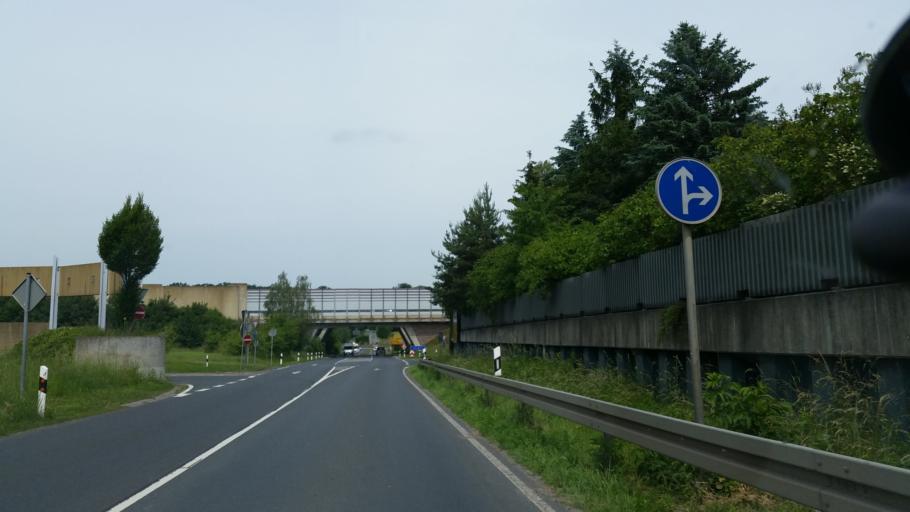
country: DE
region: Lower Saxony
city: Konigslutter am Elm
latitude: 52.3098
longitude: 10.8157
